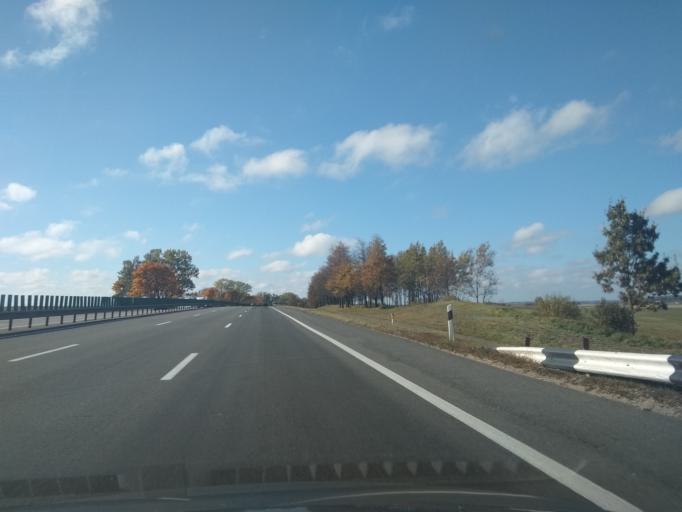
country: BY
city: Fanipol
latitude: 53.7334
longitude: 27.2989
